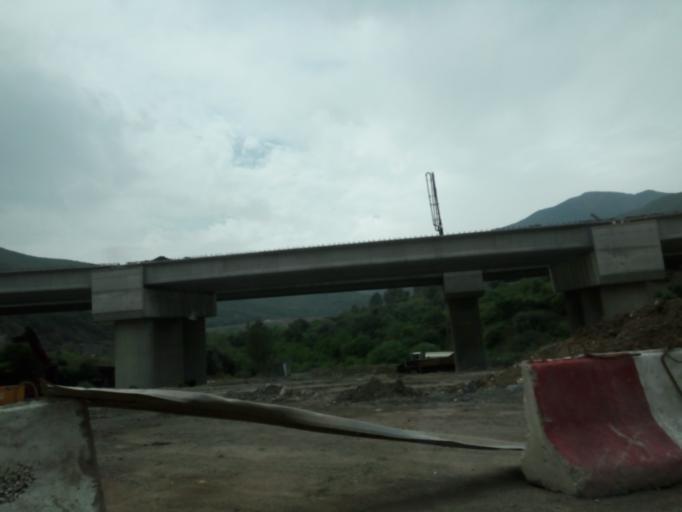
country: DZ
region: Medea
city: Medea
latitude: 36.3334
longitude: 2.7625
